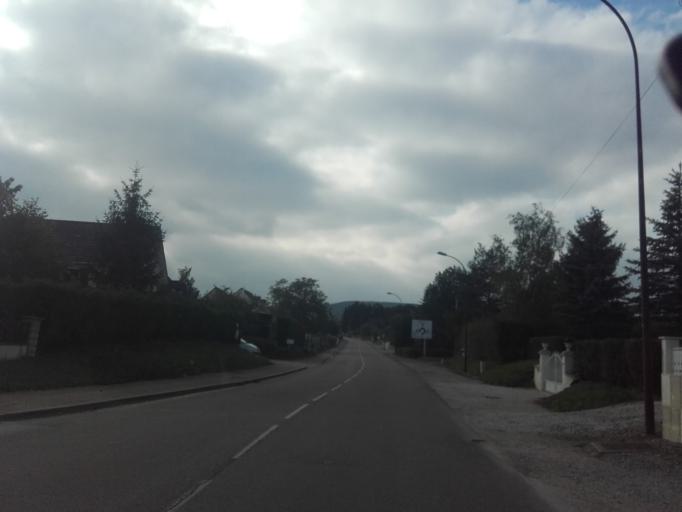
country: FR
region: Bourgogne
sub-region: Departement de Saone-et-Loire
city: Rully
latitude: 46.8799
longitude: 4.7577
